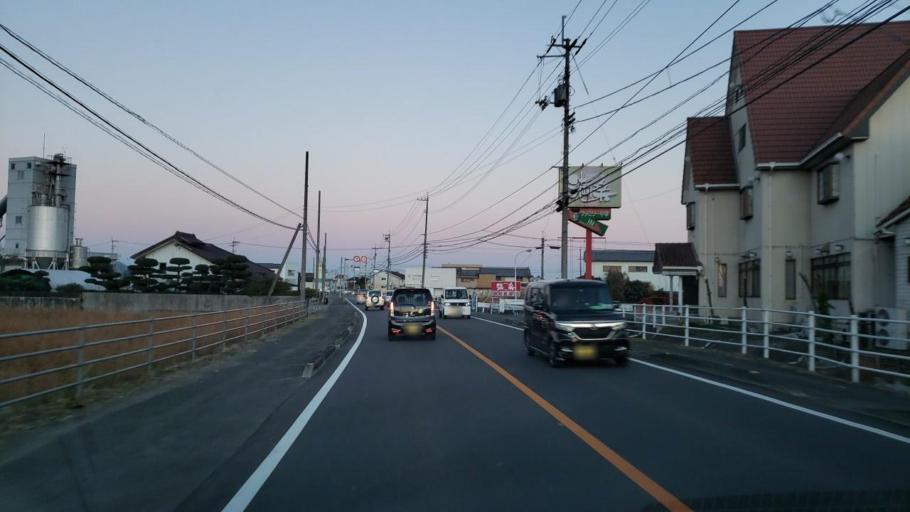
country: JP
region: Tokushima
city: Ishii
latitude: 34.1126
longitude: 134.4154
